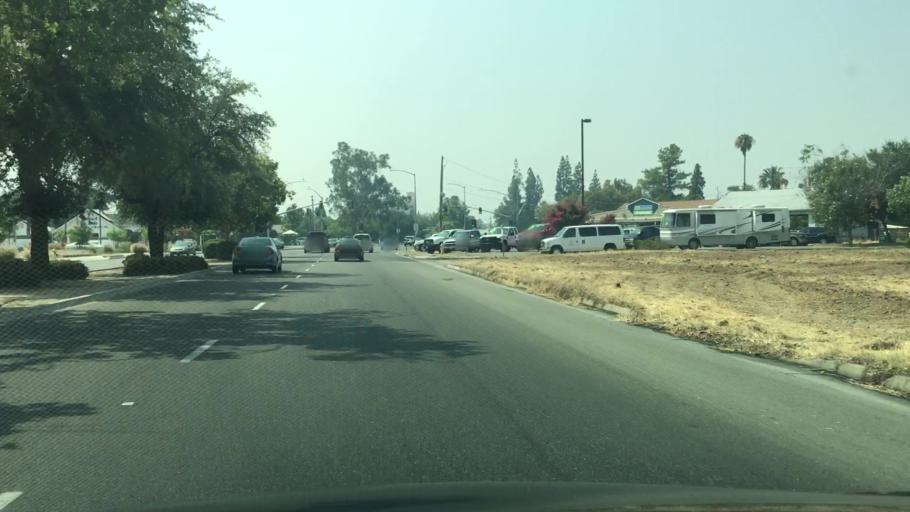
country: US
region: California
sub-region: Fresno County
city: Clovis
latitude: 36.8318
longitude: -119.7001
